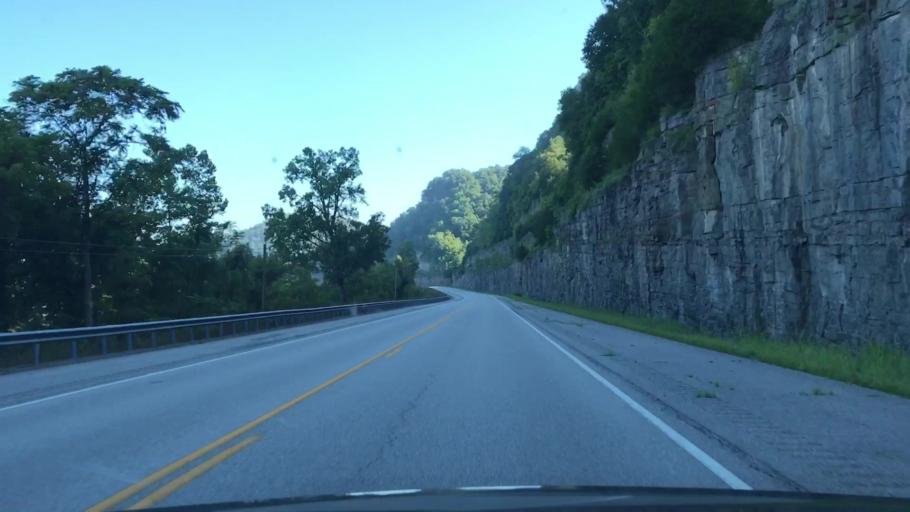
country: US
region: Tennessee
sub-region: Clay County
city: Celina
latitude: 36.4533
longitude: -85.5770
